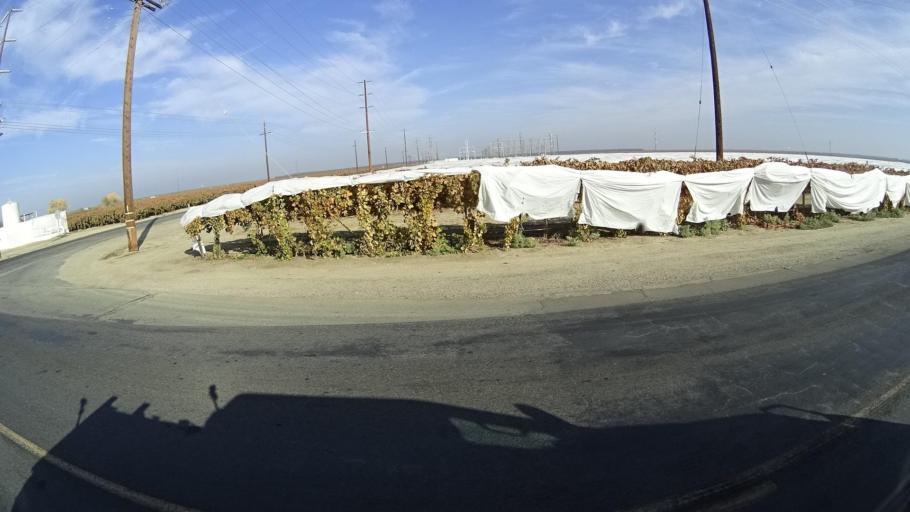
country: US
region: California
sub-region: Kern County
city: McFarland
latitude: 35.6020
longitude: -119.2041
